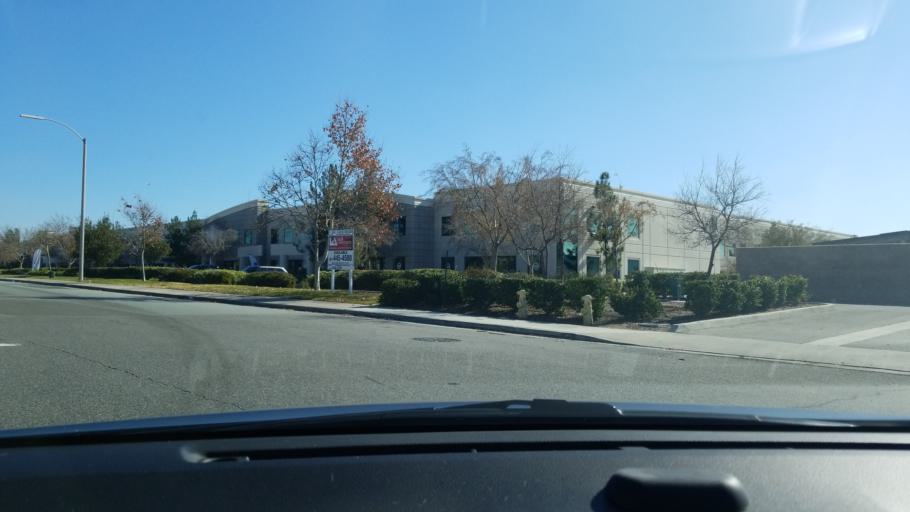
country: US
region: California
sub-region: Riverside County
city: Murrieta
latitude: 33.5905
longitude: -117.2368
